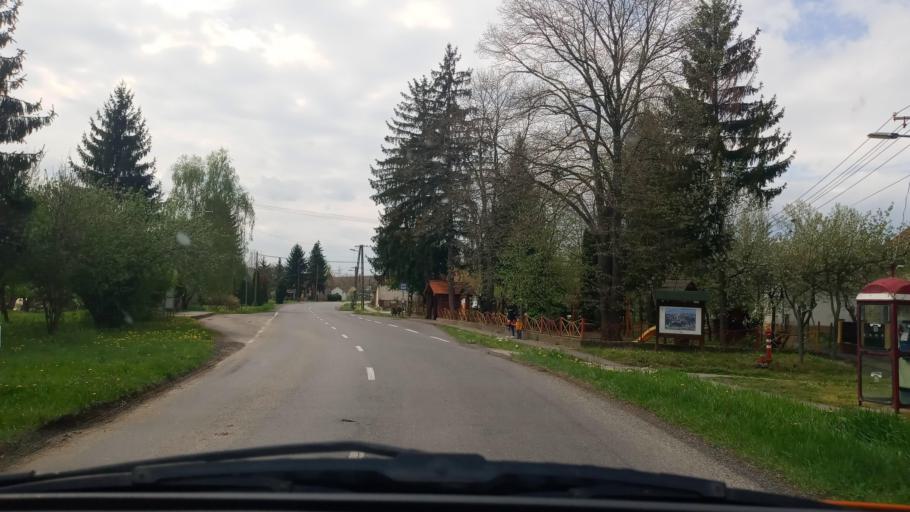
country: HU
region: Baranya
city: Sasd
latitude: 46.2713
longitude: 18.0486
